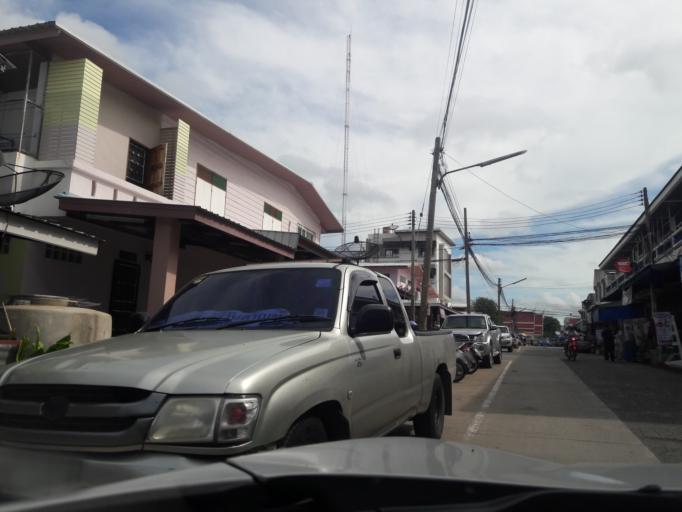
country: TH
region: Nakhon Sawan
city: Tak Fa
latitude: 15.3454
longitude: 100.4944
